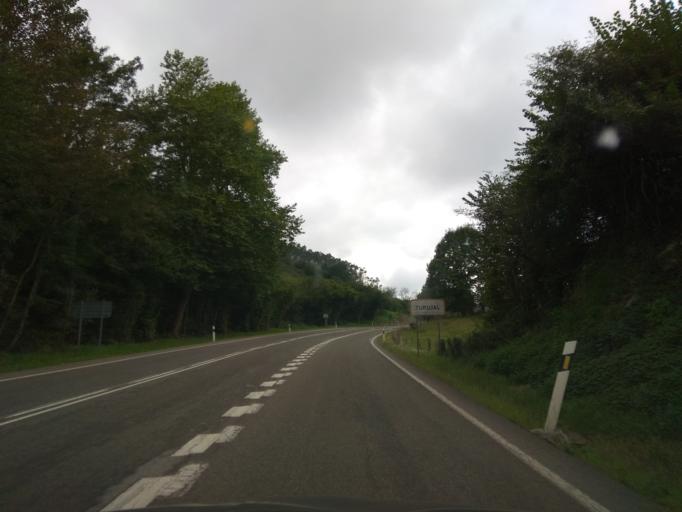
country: ES
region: Cantabria
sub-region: Provincia de Cantabria
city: Cabezon de la Sal
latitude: 43.3144
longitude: -4.2645
